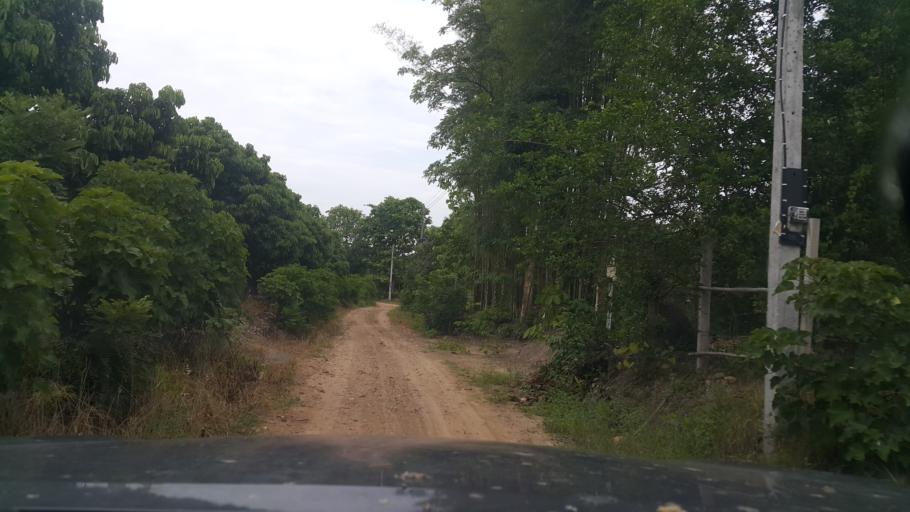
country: TH
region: Chiang Mai
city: San Pa Tong
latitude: 18.6771
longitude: 98.8413
